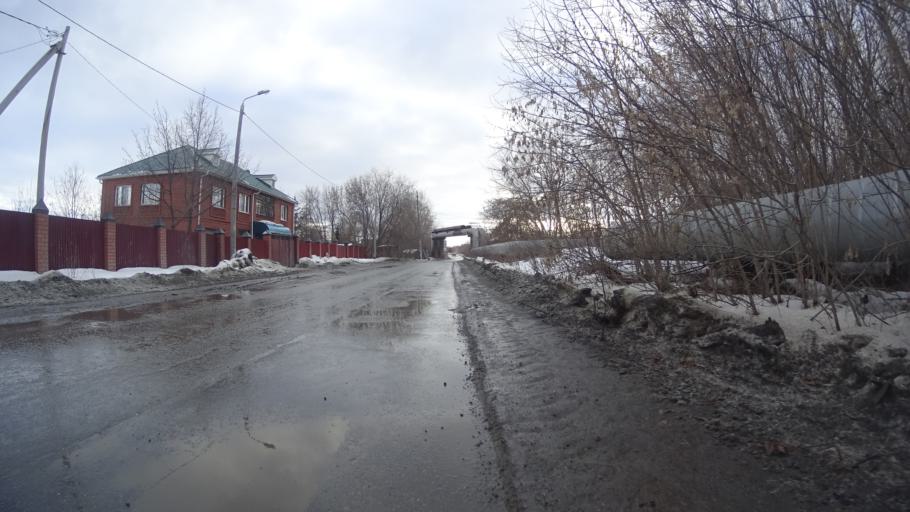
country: RU
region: Chelyabinsk
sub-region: Gorod Chelyabinsk
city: Chelyabinsk
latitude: 55.1367
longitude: 61.3928
